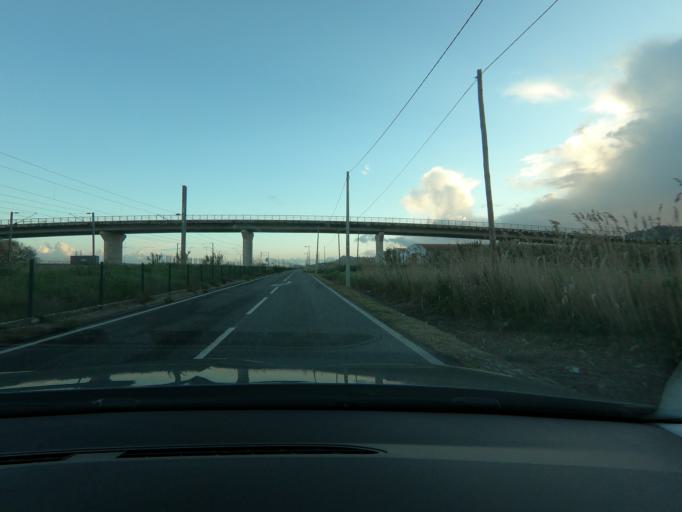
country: PT
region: Lisbon
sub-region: Vila Franca de Xira
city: Castanheira do Ribatejo
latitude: 39.0028
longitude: -8.9560
